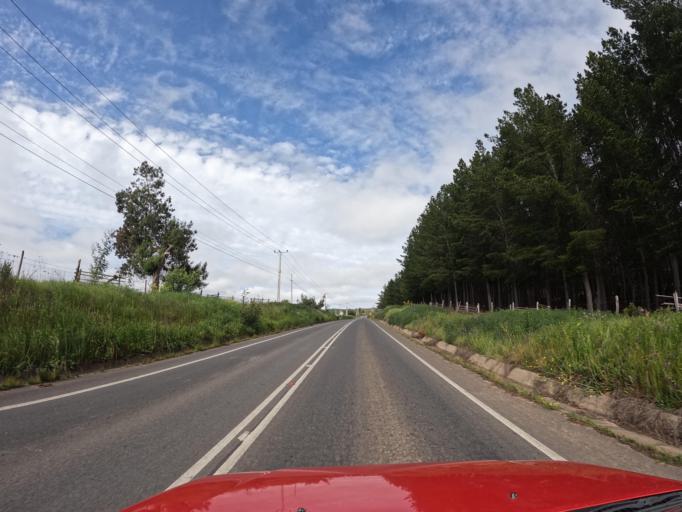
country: CL
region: O'Higgins
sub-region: Provincia de Colchagua
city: Santa Cruz
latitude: -34.3495
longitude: -71.9357
